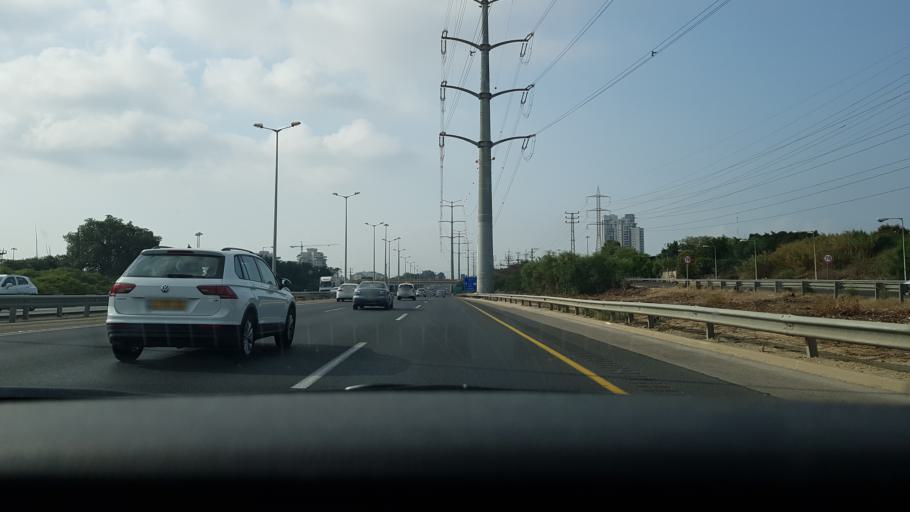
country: IL
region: Central District
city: Rishon LeZiyyon
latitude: 31.9810
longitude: 34.7939
